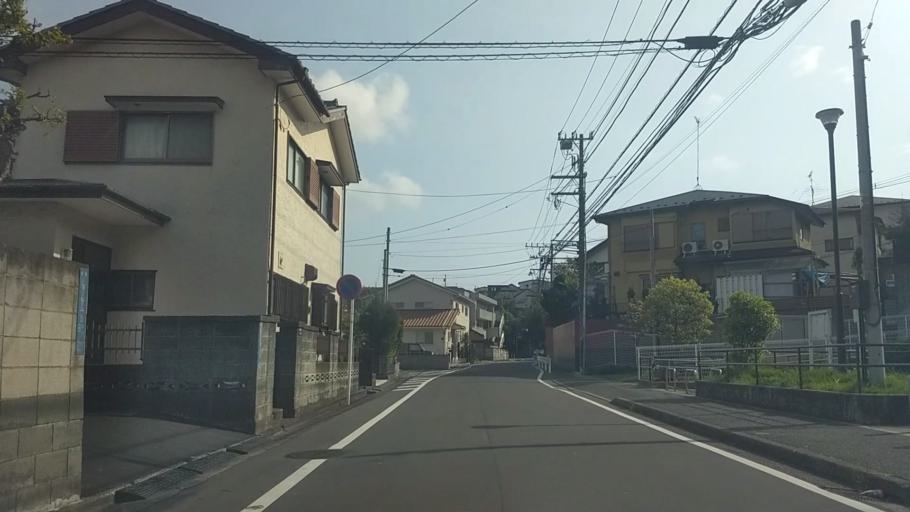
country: JP
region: Kanagawa
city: Kamakura
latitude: 35.3736
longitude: 139.5539
